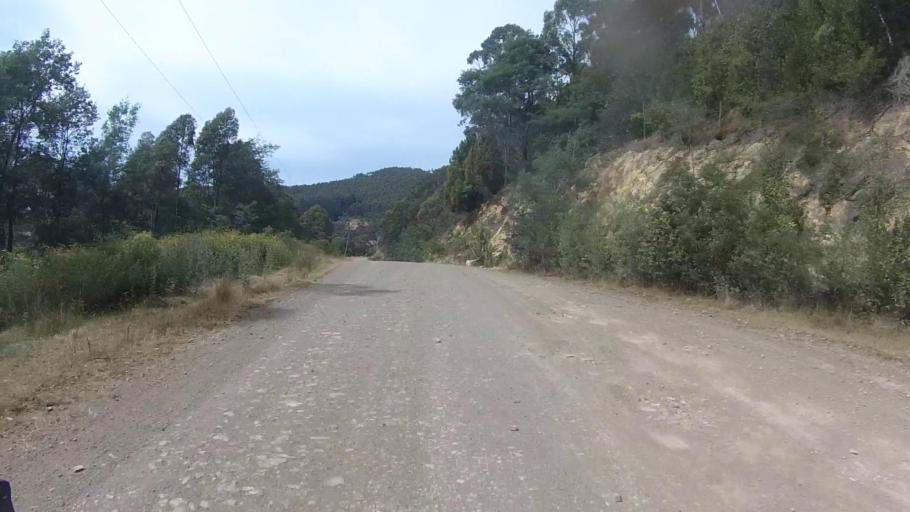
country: AU
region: Tasmania
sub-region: Sorell
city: Sorell
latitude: -42.7714
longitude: 147.8301
